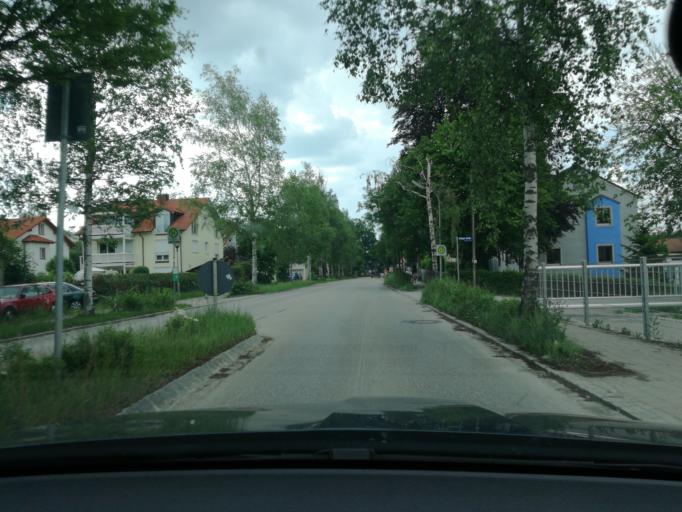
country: DE
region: Bavaria
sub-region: Upper Bavaria
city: Schondorf am Ammersee
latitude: 48.0469
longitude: 11.0907
